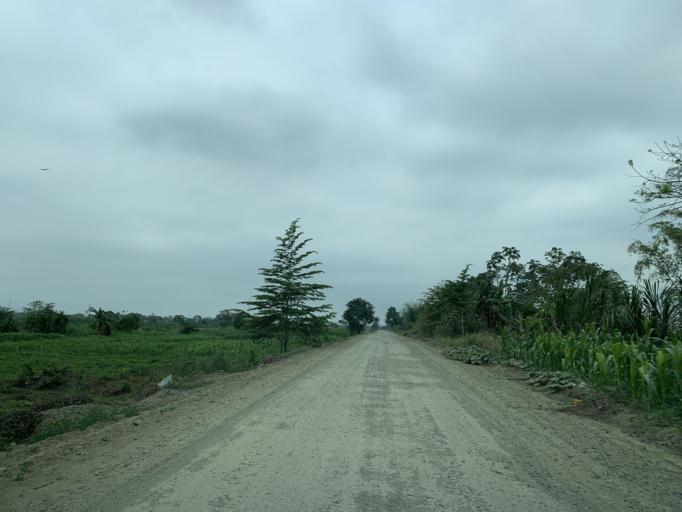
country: EC
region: Canar
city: La Troncal
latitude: -2.3706
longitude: -79.4371
